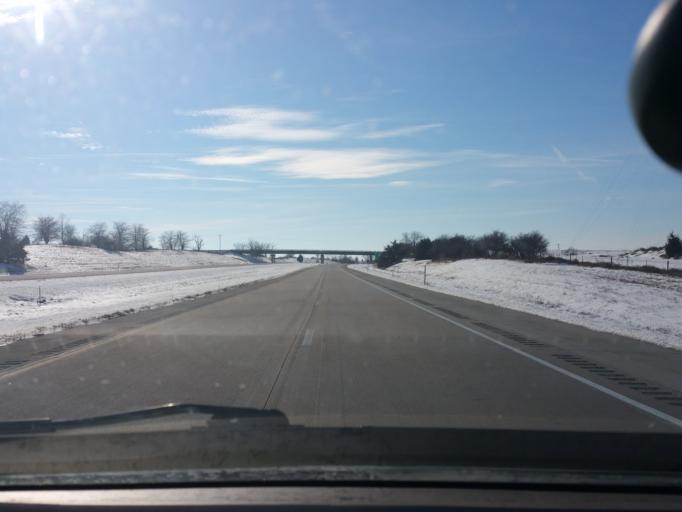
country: US
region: Iowa
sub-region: Decatur County
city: Leon
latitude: 40.7612
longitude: -93.8369
